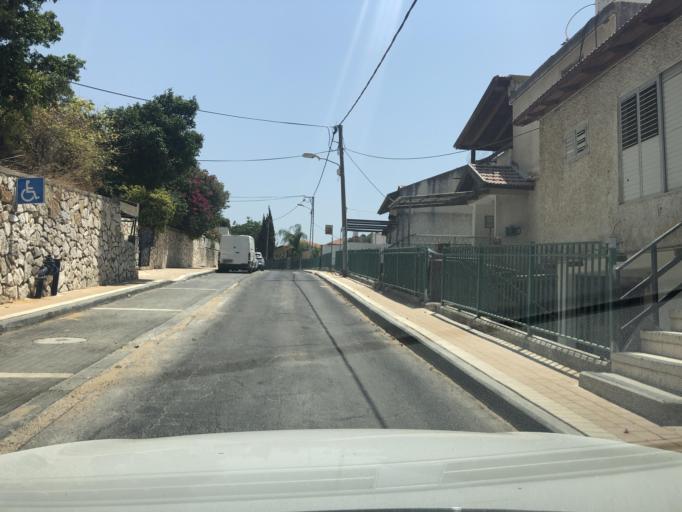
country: IL
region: Haifa
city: Daliyat el Karmil
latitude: 32.6607
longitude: 35.1081
